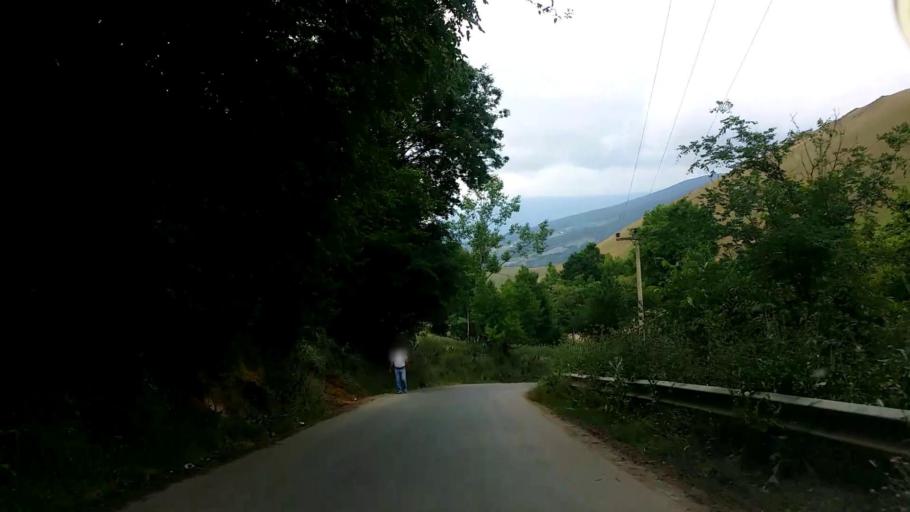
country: IR
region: Mazandaran
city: Chalus
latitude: 36.5198
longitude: 51.2601
